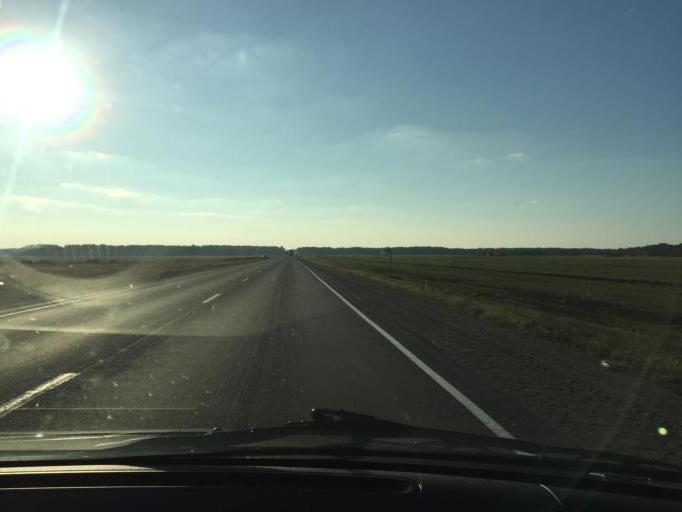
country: BY
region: Brest
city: Horad Luninyets
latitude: 52.3000
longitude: 26.4596
